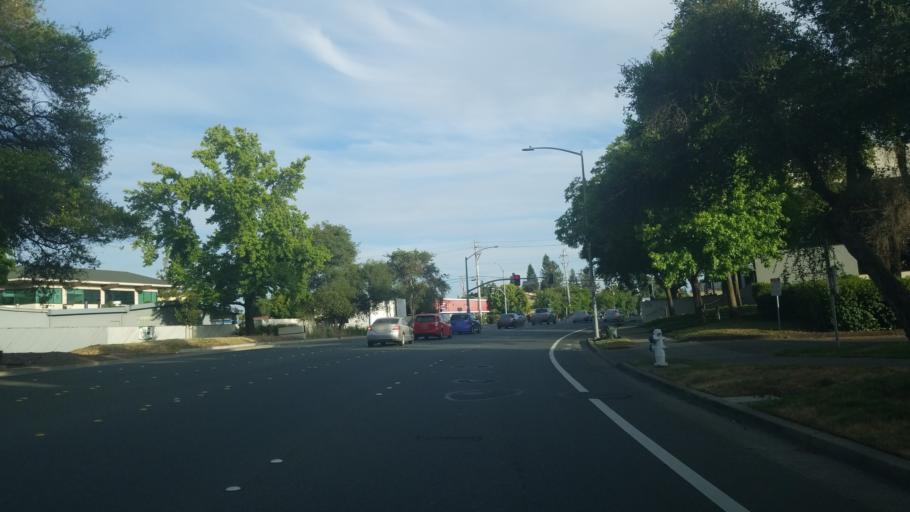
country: US
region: California
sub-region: Sonoma County
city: Santa Rosa
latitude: 38.4467
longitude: -122.7307
